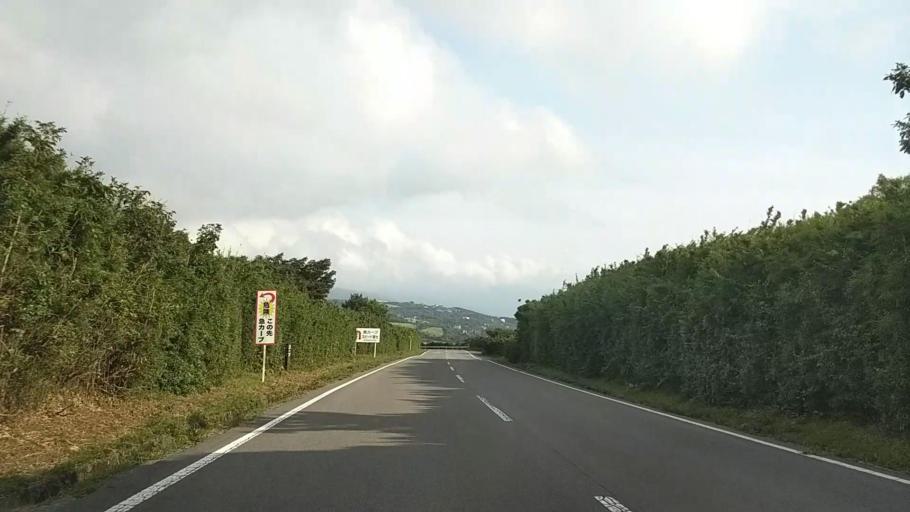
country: JP
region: Kanagawa
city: Hakone
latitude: 35.1948
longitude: 138.9962
